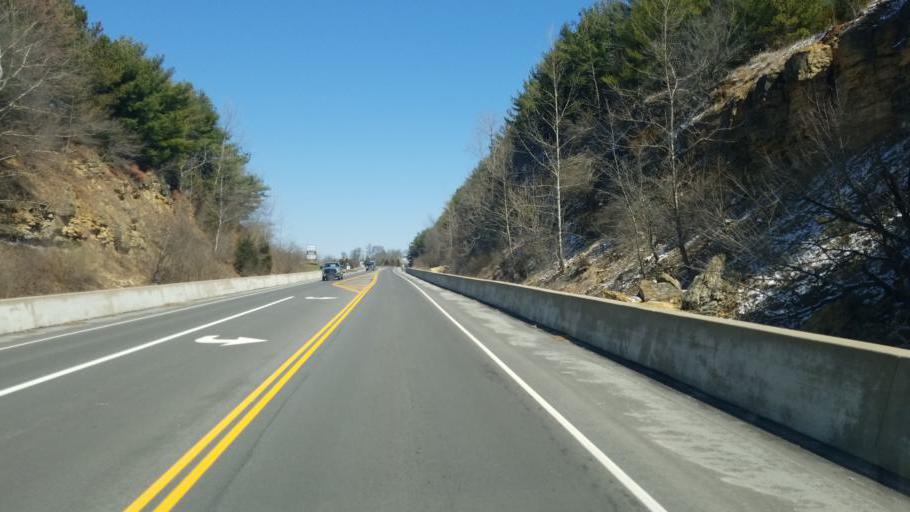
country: US
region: Ohio
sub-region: Highland County
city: Hillsboro
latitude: 39.1868
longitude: -83.6162
